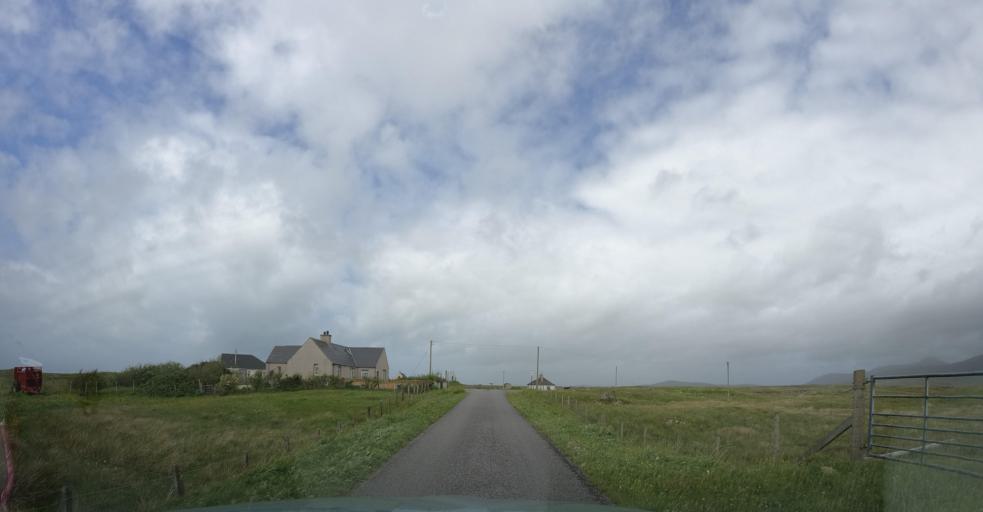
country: GB
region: Scotland
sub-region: Eilean Siar
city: Isle of South Uist
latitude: 57.2468
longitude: -7.4046
